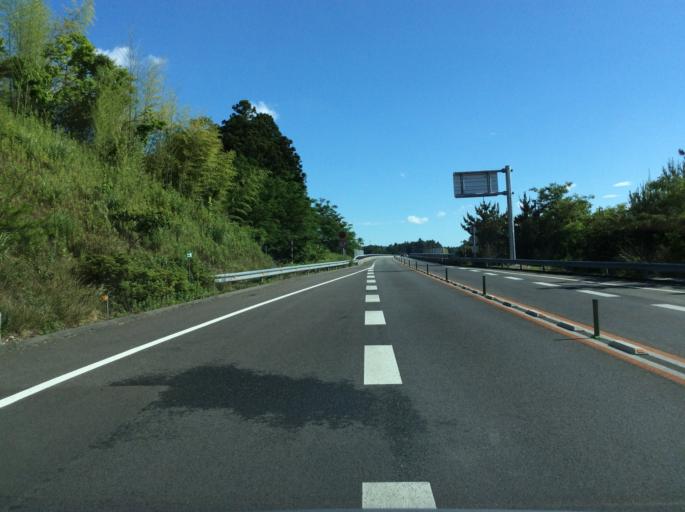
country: JP
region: Fukushima
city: Namie
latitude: 37.2893
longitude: 140.9822
